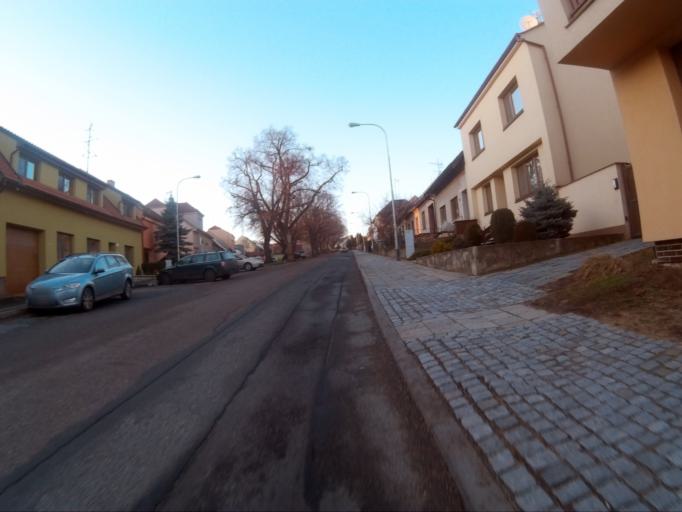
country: CZ
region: South Moravian
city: Ostopovice
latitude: 49.1743
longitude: 16.5325
